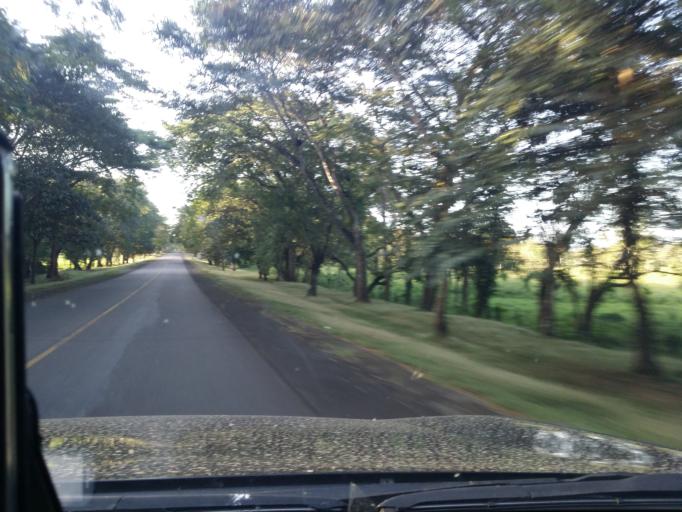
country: NI
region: Rio San Juan
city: San Miguelito
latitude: 11.4110
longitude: -84.8369
